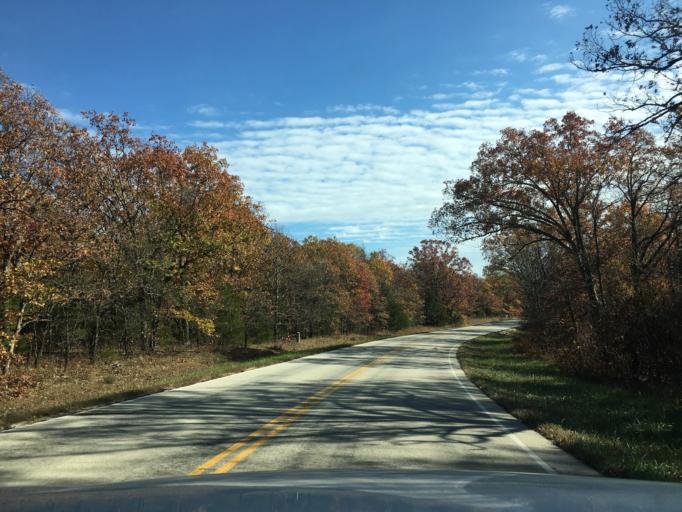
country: US
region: Missouri
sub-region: Maries County
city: Belle
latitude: 38.3169
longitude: -91.7490
